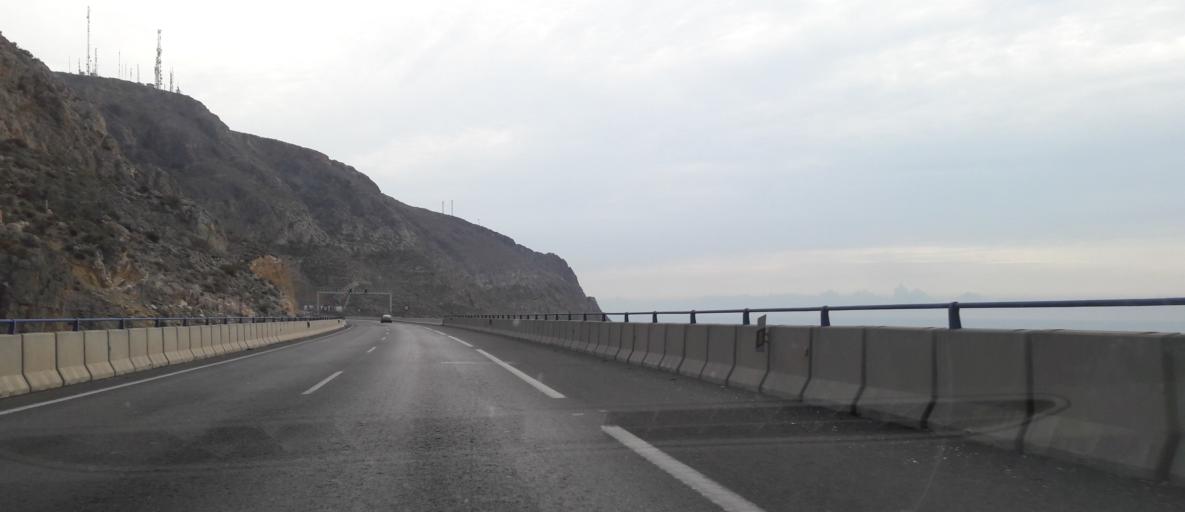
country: ES
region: Andalusia
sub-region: Provincia de Almeria
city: Aguadulce
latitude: 36.8212
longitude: -2.5696
